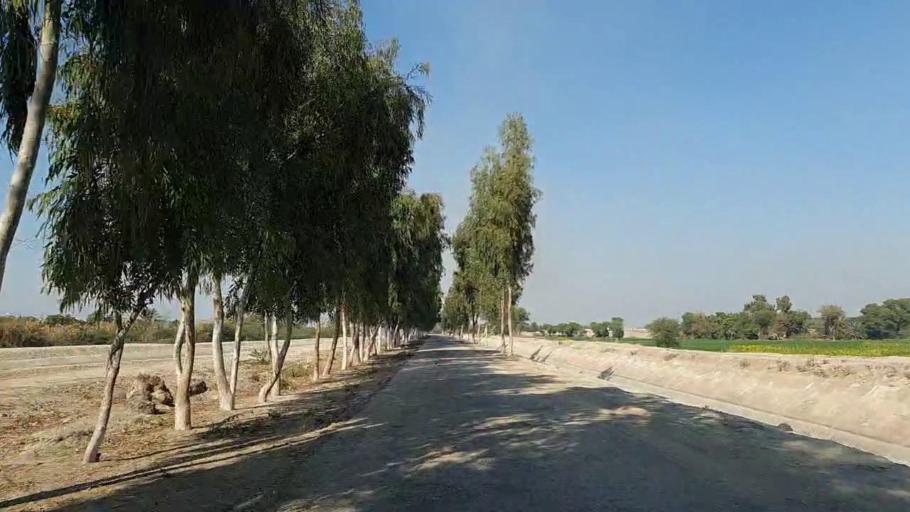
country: PK
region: Sindh
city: Nawabshah
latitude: 26.3447
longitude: 68.3814
